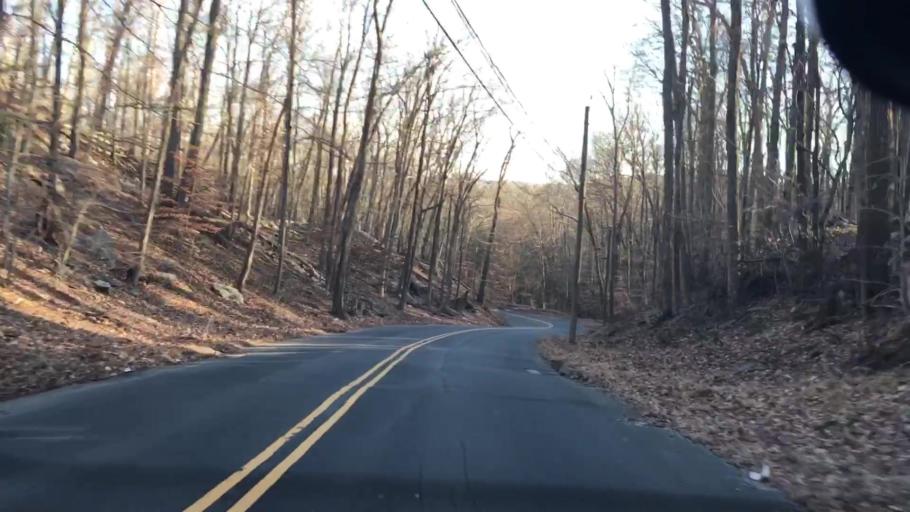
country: US
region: Connecticut
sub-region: Fairfield County
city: Newtown
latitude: 41.4662
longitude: -73.3354
